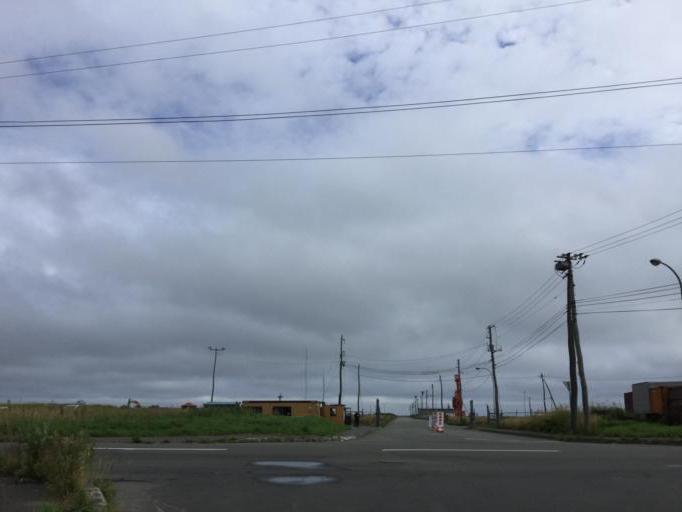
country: JP
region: Hokkaido
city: Wakkanai
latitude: 45.4012
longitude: 141.6903
